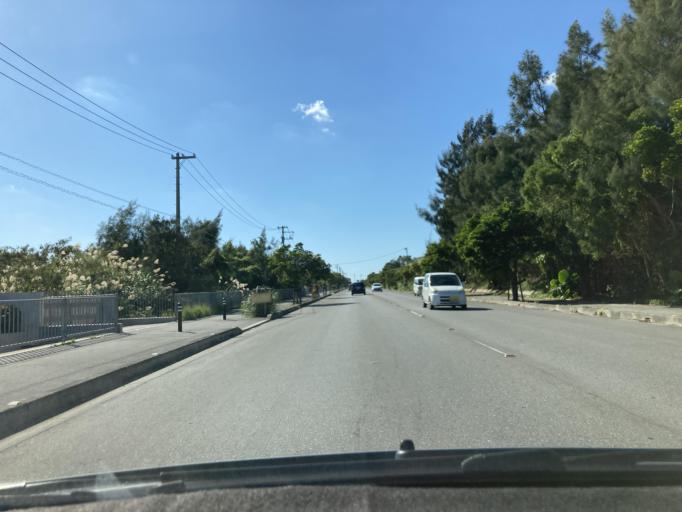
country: JP
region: Okinawa
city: Gushikawa
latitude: 26.3795
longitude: 127.8358
